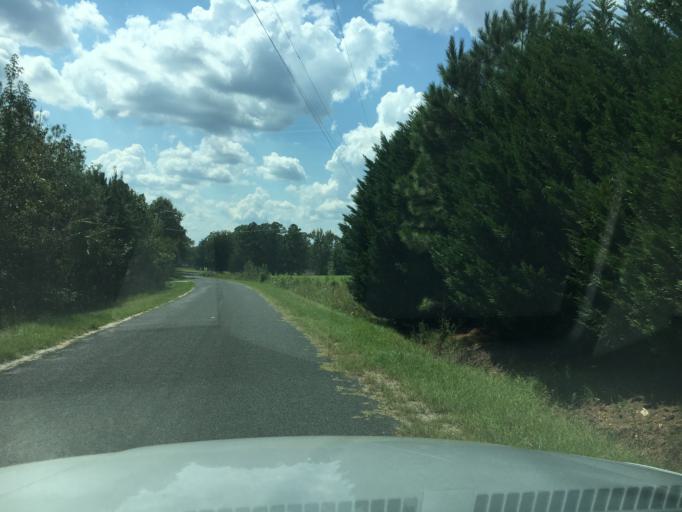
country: US
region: South Carolina
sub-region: Greenwood County
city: Greenwood
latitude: 34.0615
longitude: -82.1531
